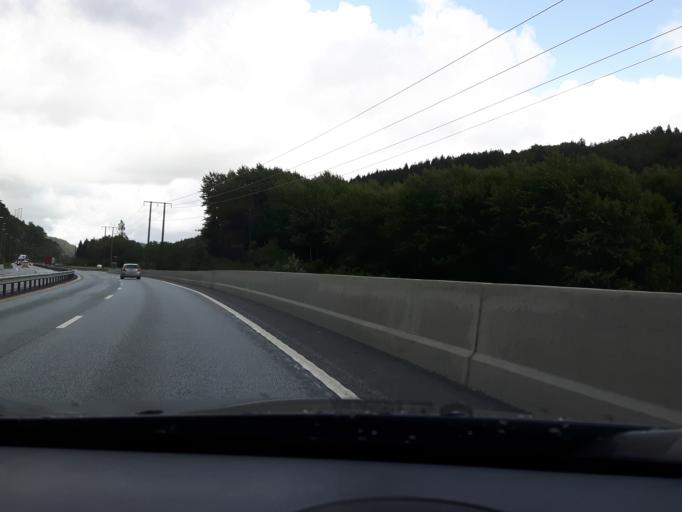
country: NO
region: Vest-Agder
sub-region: Sogne
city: Tangvall
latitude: 58.1085
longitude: 7.8311
